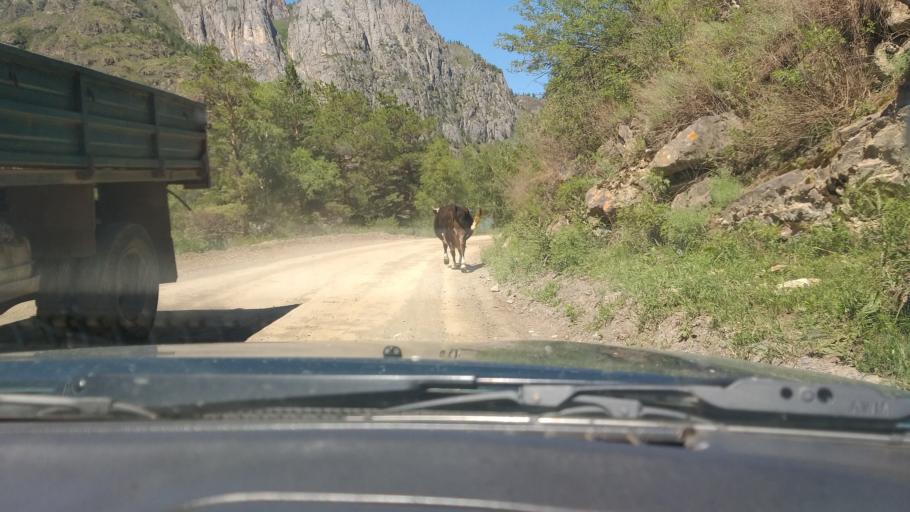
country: RU
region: Altay
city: Chemal
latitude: 51.2032
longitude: 86.0853
